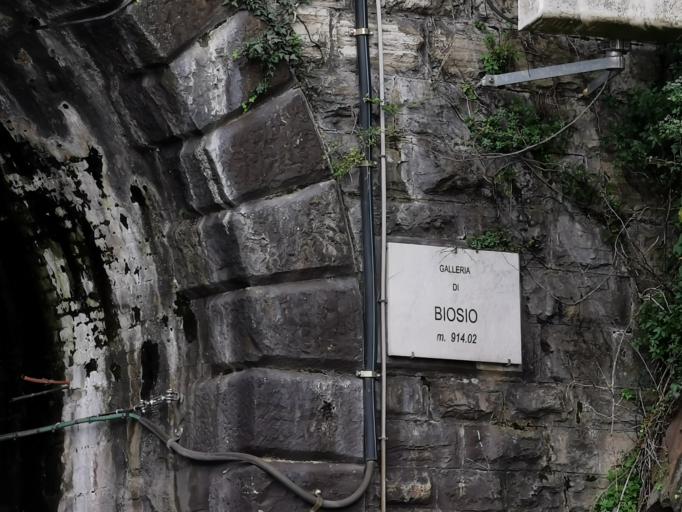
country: IT
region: Lombardy
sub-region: Provincia di Lecco
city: Perledo
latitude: 46.0320
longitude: 9.2944
